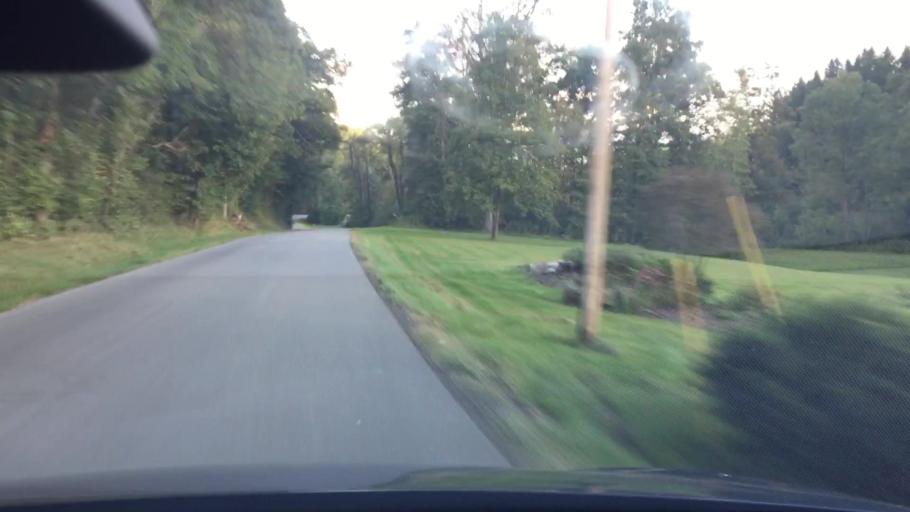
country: US
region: Pennsylvania
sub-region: Butler County
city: Nixon
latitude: 40.7799
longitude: -79.8890
